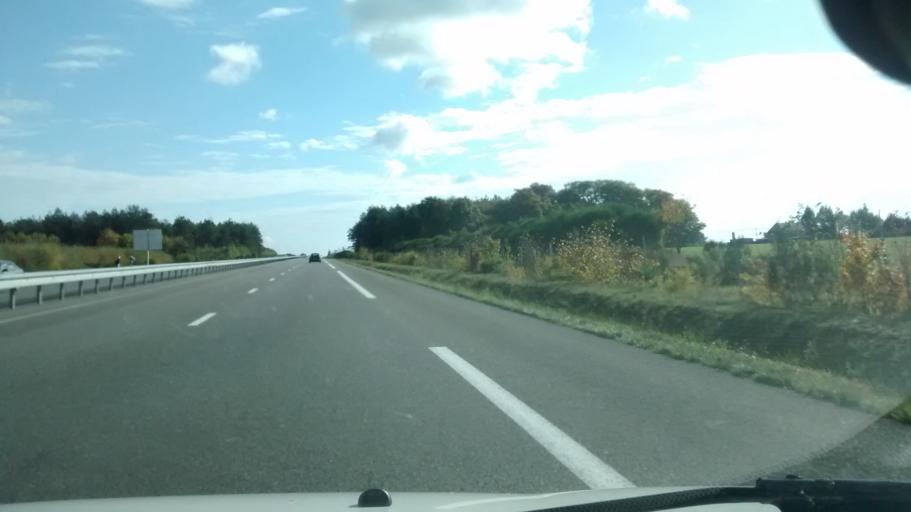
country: FR
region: Pays de la Loire
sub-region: Departement de Maine-et-Loire
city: Combree
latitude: 47.7281
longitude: -1.0631
